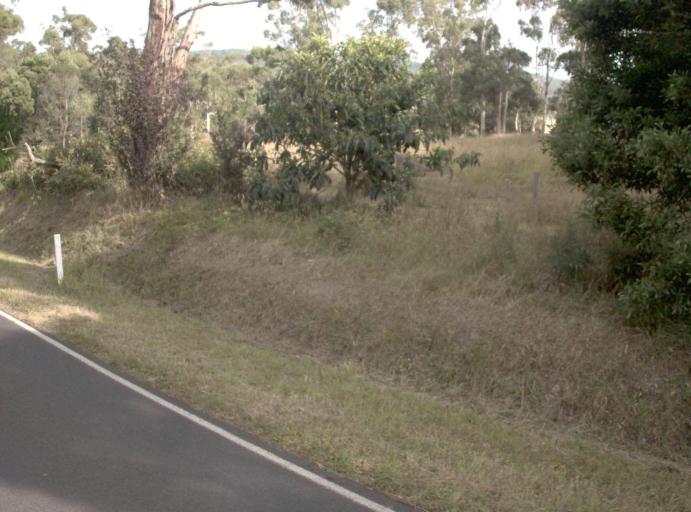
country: AU
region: Victoria
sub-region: Latrobe
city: Morwell
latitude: -38.2781
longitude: 146.3024
